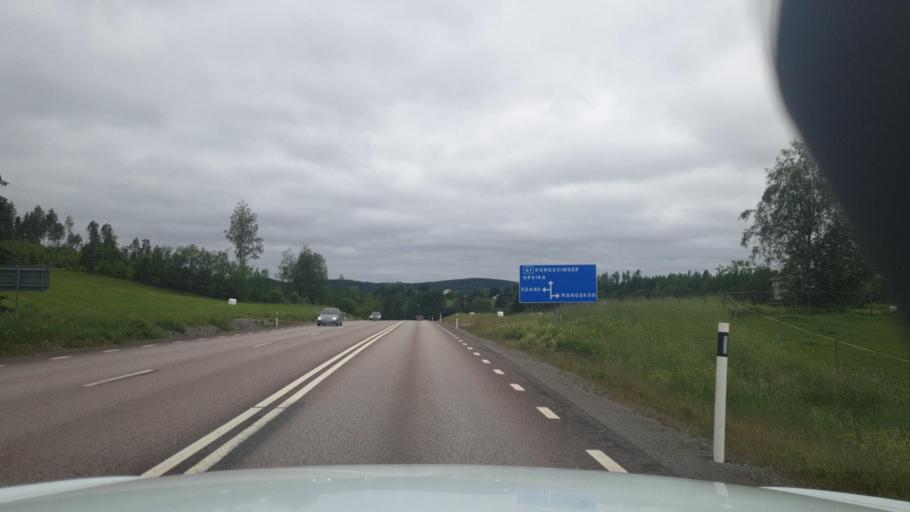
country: SE
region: Vaermland
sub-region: Arvika Kommun
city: Arvika
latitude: 59.6682
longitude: 12.8057
